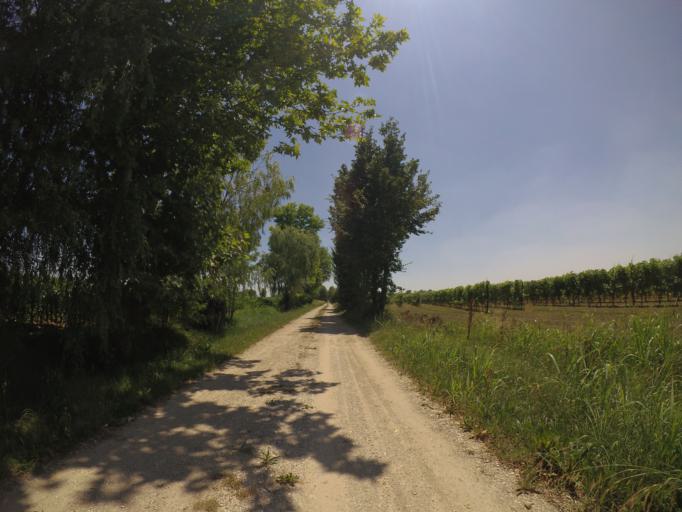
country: IT
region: Friuli Venezia Giulia
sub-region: Provincia di Udine
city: Bertiolo
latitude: 45.9429
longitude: 13.0162
